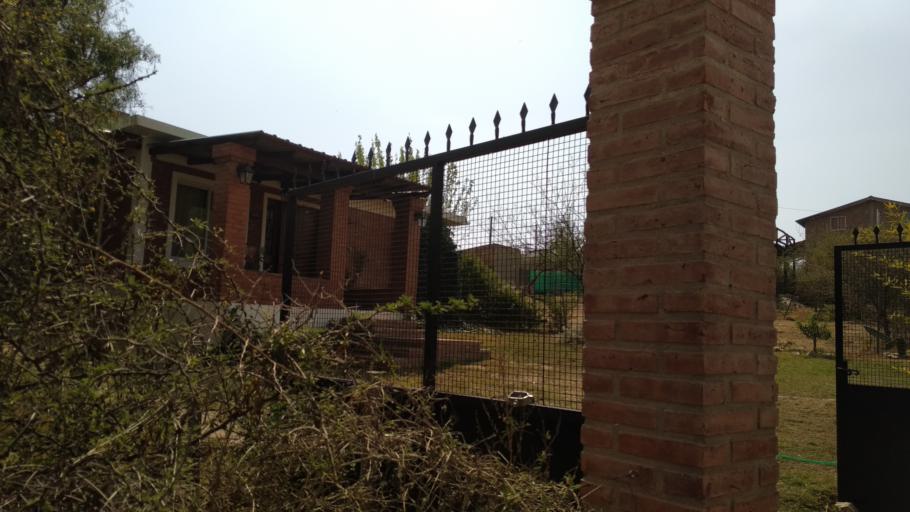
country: AR
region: Cordoba
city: Mina Clavero
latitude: -31.7635
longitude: -64.9967
